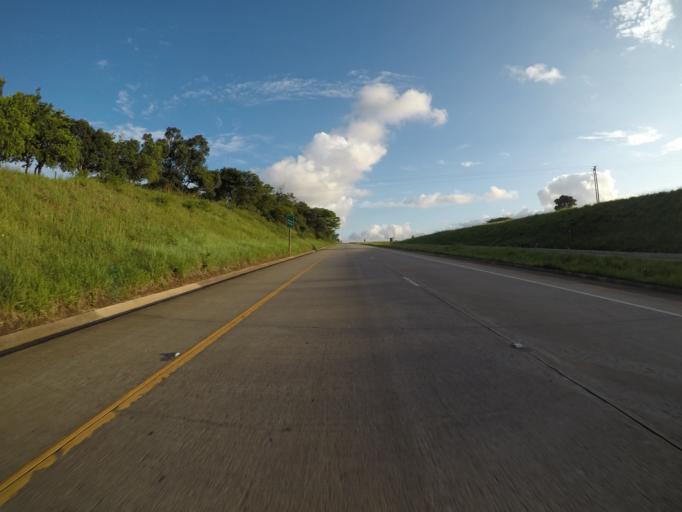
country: ZA
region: KwaZulu-Natal
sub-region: uMkhanyakude District Municipality
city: Mtubatuba
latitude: -28.5060
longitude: 32.1376
